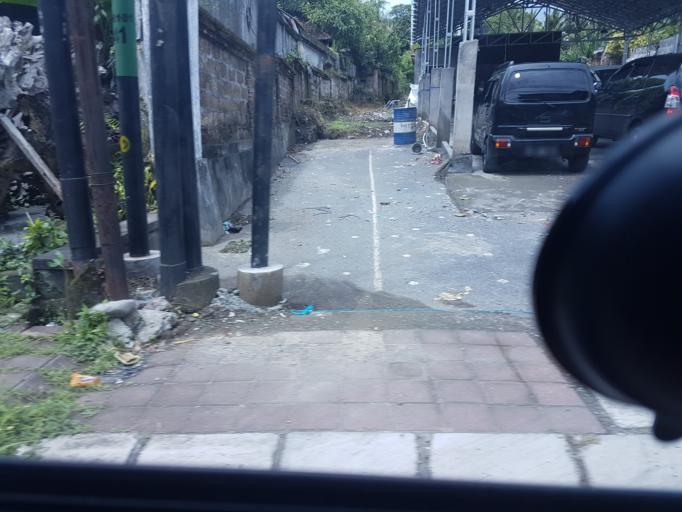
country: ID
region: Bali
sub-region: Kabupaten Gianyar
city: Ubud
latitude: -8.5355
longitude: 115.2726
